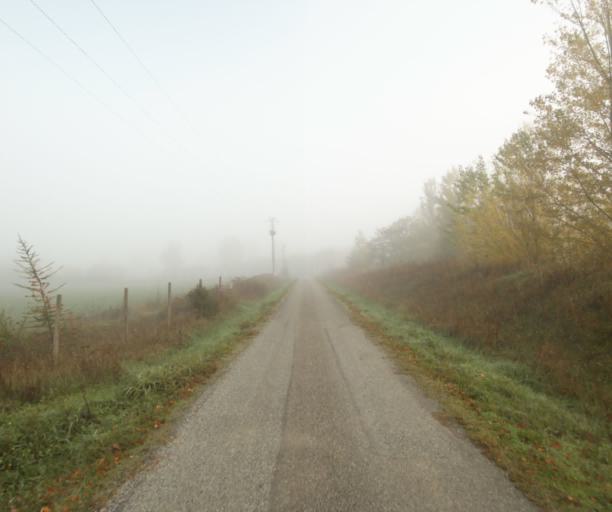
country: FR
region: Midi-Pyrenees
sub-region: Departement du Tarn-et-Garonne
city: Nohic
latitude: 43.8989
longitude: 1.4590
